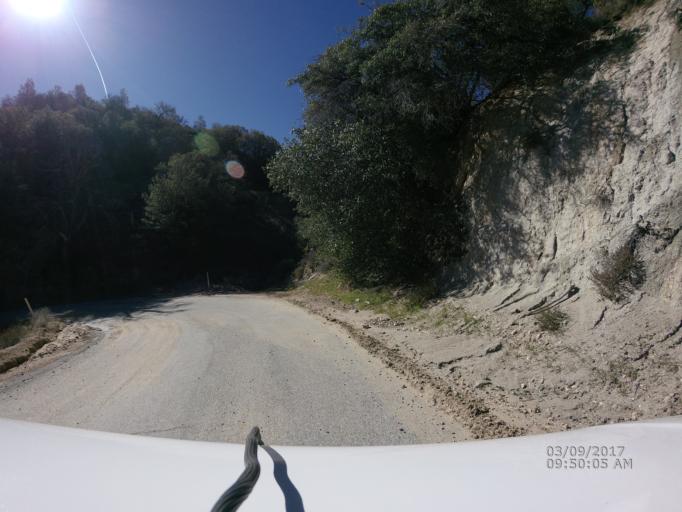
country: US
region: California
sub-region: Kern County
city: Lebec
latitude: 34.7447
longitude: -118.7083
